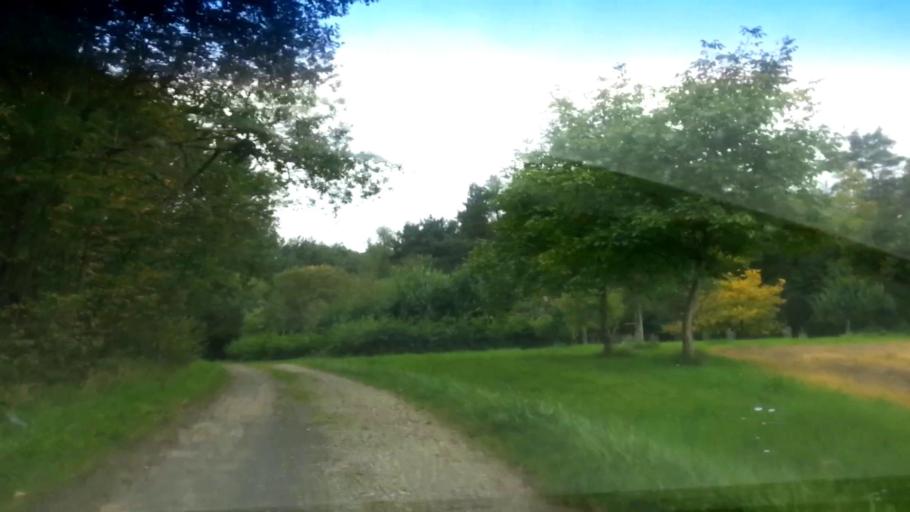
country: DE
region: Bavaria
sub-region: Upper Franconia
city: Zapfendorf
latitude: 50.0039
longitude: 10.9311
